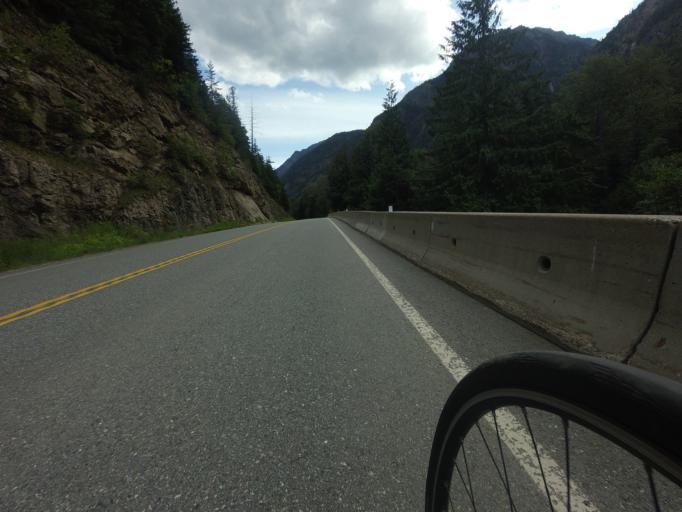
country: CA
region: British Columbia
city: Lillooet
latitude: 50.6225
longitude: -122.1031
